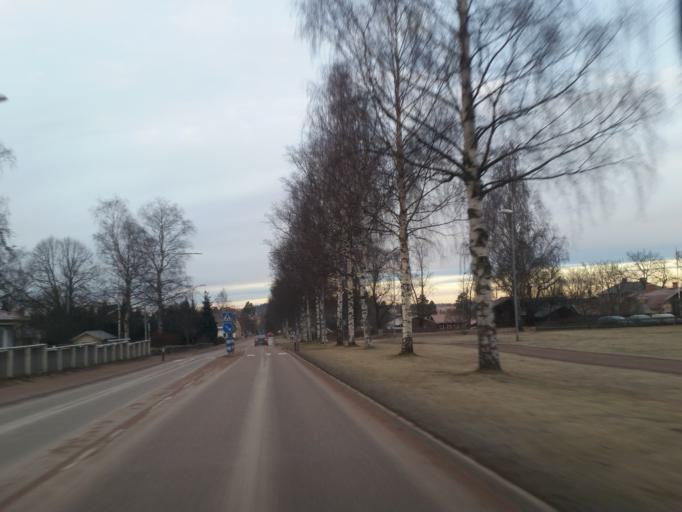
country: SE
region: Dalarna
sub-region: Leksand Municipality
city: Leksand
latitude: 60.7240
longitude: 15.0021
